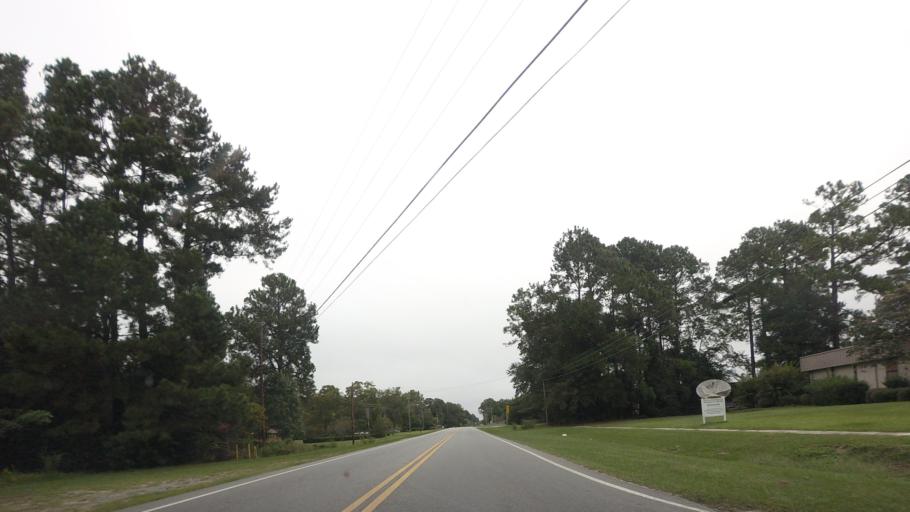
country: US
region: Georgia
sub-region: Berrien County
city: Nashville
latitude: 31.2172
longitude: -83.2490
